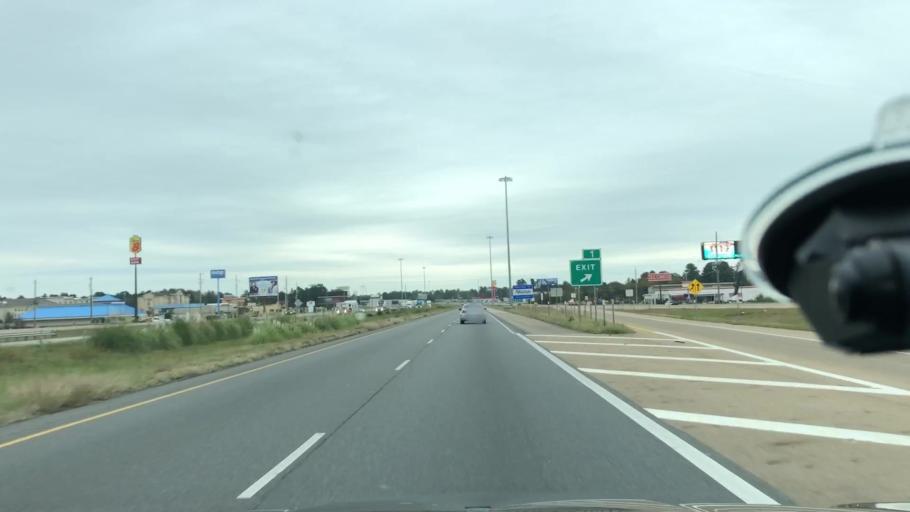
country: US
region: Arkansas
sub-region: Miller County
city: Texarkana
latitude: 33.4701
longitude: -94.0414
